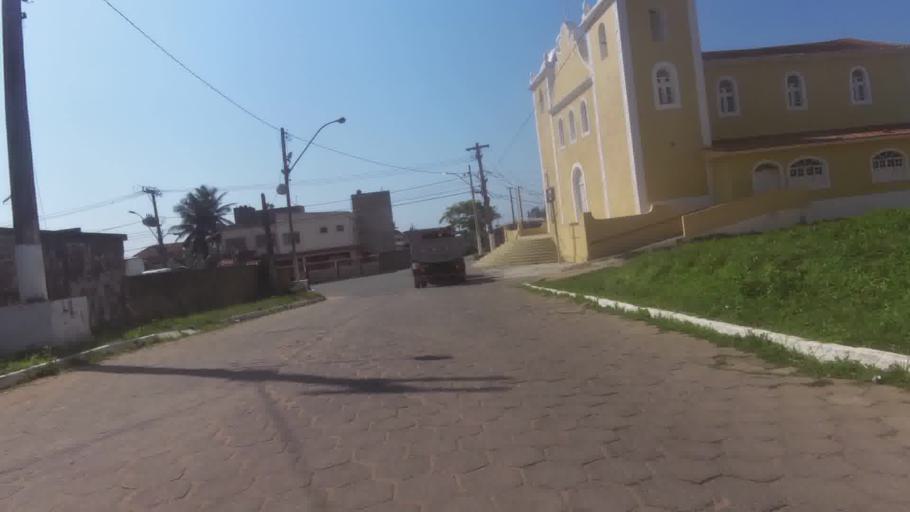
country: BR
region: Espirito Santo
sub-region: Itapemirim
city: Itapemirim
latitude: -21.0083
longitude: -40.8073
